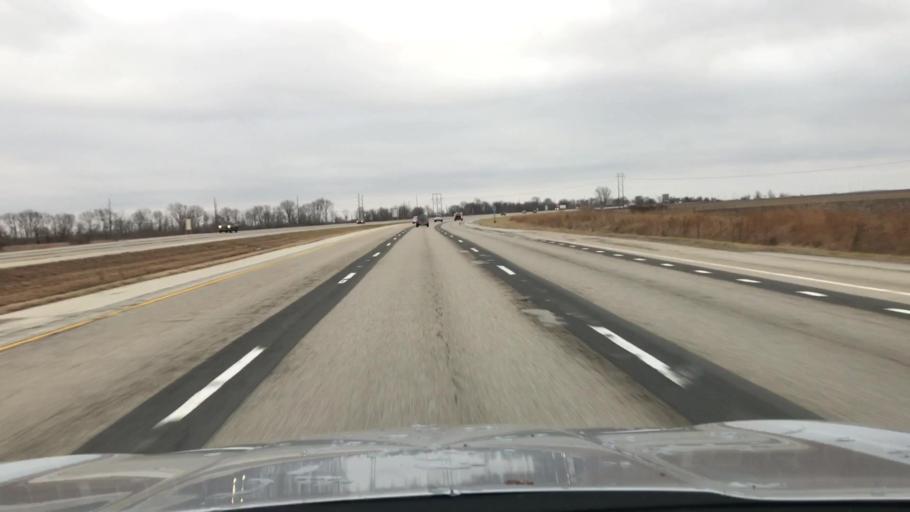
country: US
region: Illinois
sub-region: Logan County
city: Lincoln
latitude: 40.1054
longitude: -89.4165
